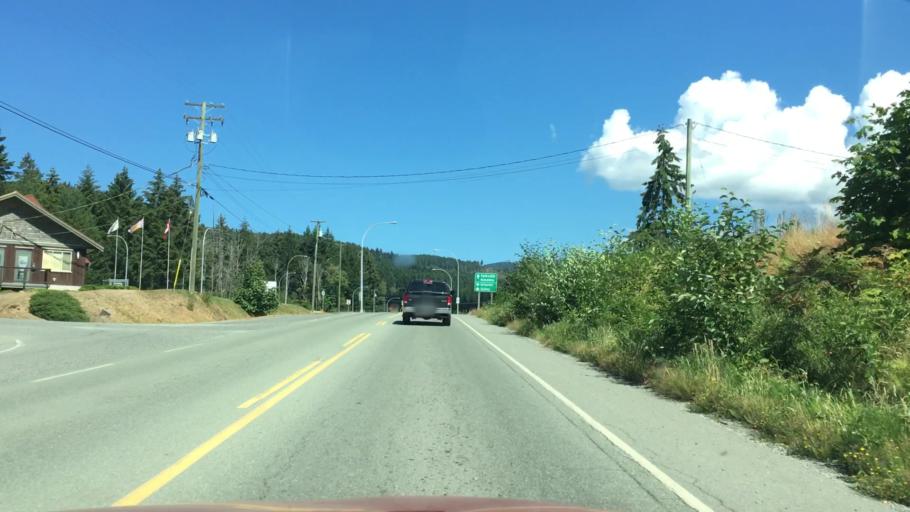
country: CA
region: British Columbia
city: Port Alberni
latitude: 49.2638
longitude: -124.7600
